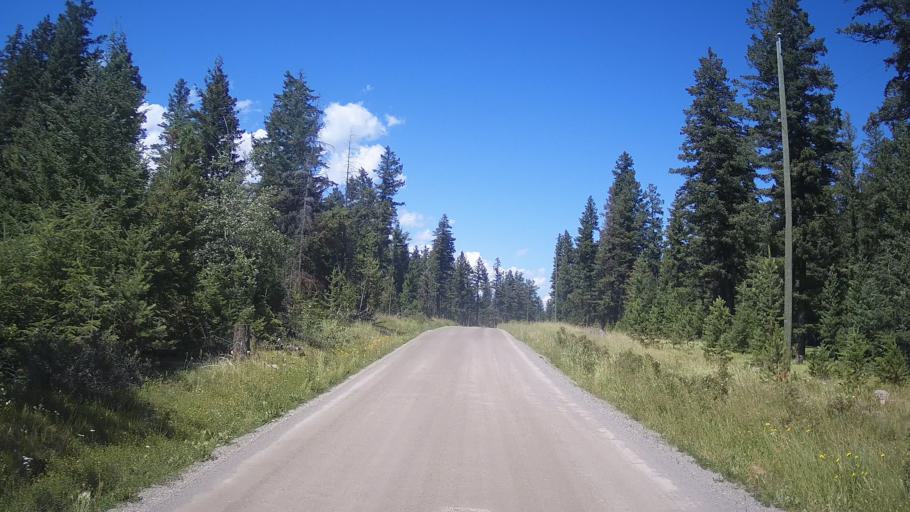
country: CA
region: British Columbia
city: Cache Creek
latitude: 51.2117
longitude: -121.6012
